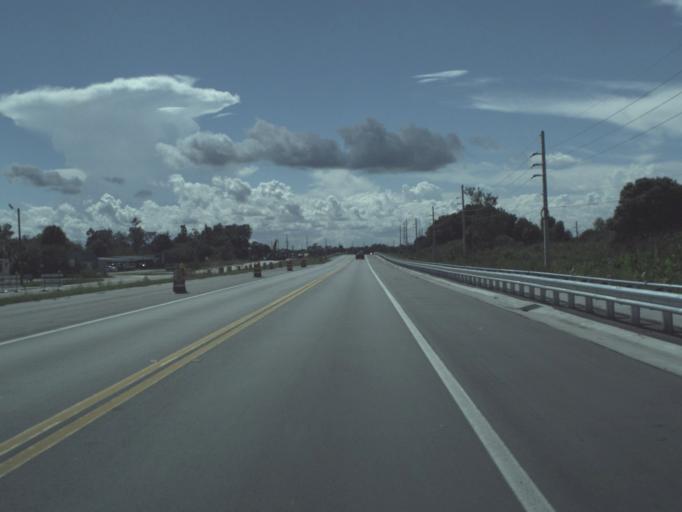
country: US
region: Florida
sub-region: Okeechobee County
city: Taylor Creek
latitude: 27.2550
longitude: -80.7667
